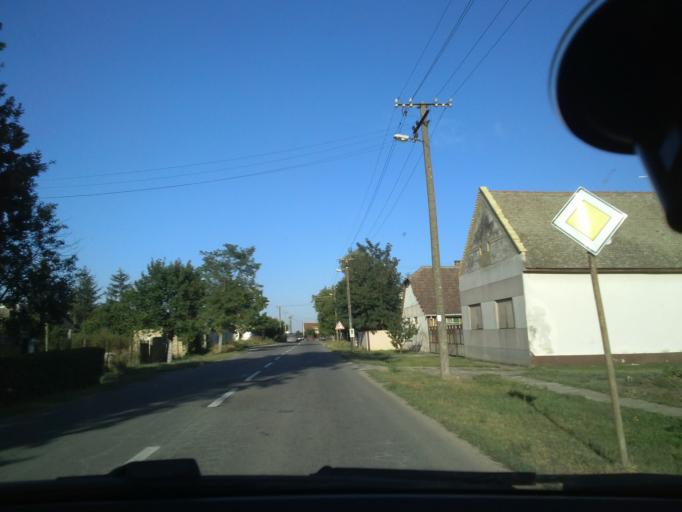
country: RS
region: Autonomna Pokrajina Vojvodina
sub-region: Zapadnobacki Okrug
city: Odzaci
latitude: 45.4507
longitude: 19.3397
